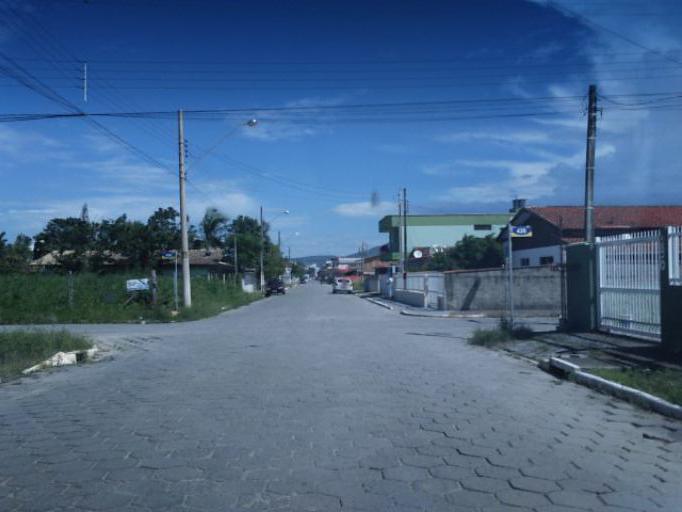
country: BR
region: Santa Catarina
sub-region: Itapema
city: Itapema
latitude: -27.1237
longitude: -48.6142
